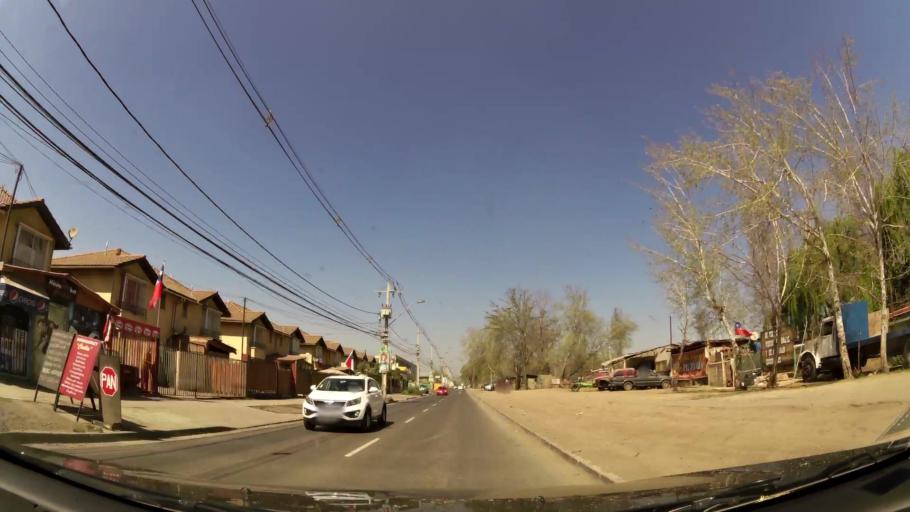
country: CL
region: Santiago Metropolitan
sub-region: Provincia de Santiago
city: Lo Prado
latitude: -33.3534
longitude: -70.7386
